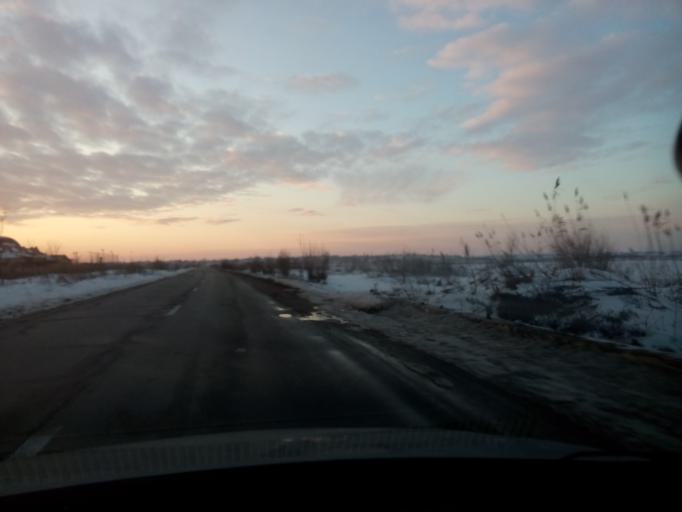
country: RO
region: Calarasi
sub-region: Comuna Budesti
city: Budesti
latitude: 44.2301
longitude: 26.4356
